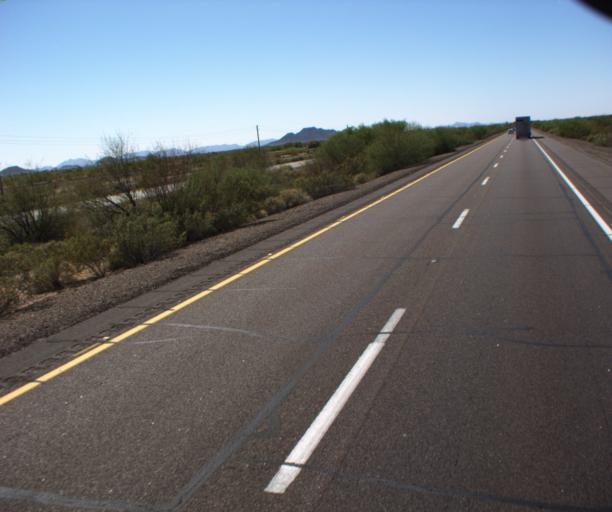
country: US
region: Arizona
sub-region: Maricopa County
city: Gila Bend
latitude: 32.8293
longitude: -113.4071
